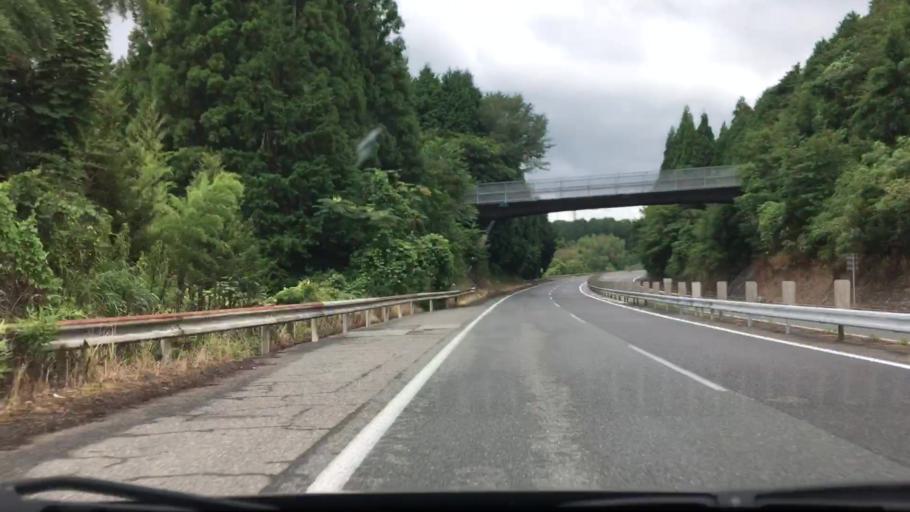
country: JP
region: Okayama
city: Niimi
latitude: 34.9306
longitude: 133.3273
